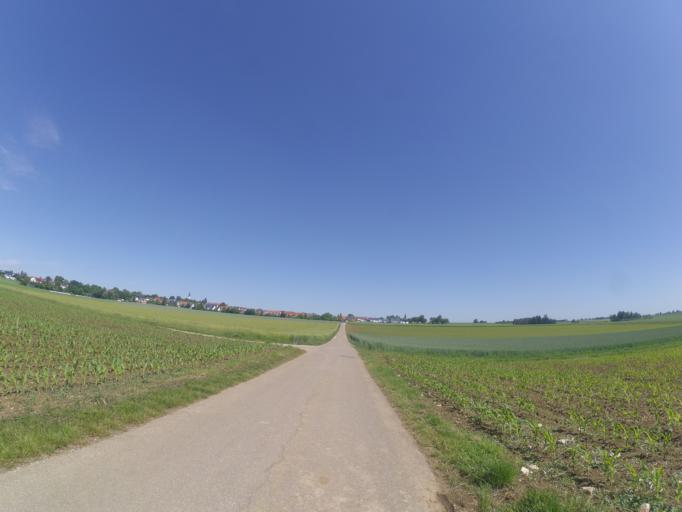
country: DE
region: Baden-Wuerttemberg
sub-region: Tuebingen Region
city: Dornstadt
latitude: 48.4760
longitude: 9.9157
